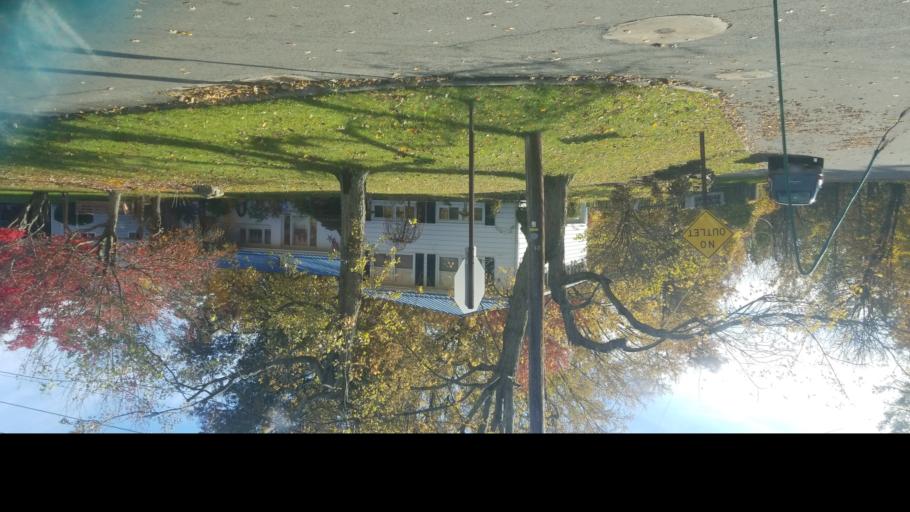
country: US
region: Ohio
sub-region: Richland County
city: Mansfield
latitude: 40.7262
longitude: -82.5288
